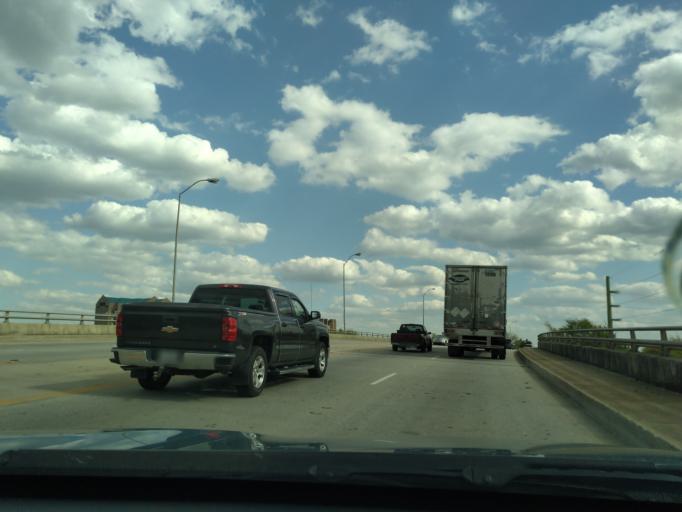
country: US
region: South Carolina
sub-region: Florence County
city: Florence
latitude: 34.1997
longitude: -79.7628
